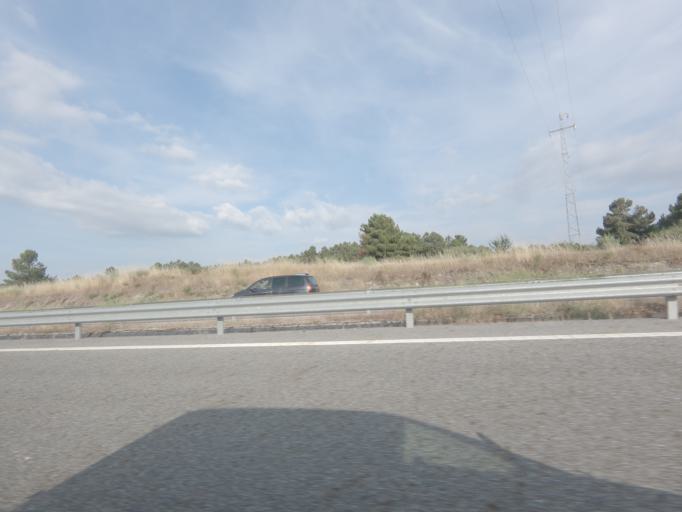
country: PT
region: Vila Real
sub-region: Chaves
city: Chaves
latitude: 41.7516
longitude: -7.5192
